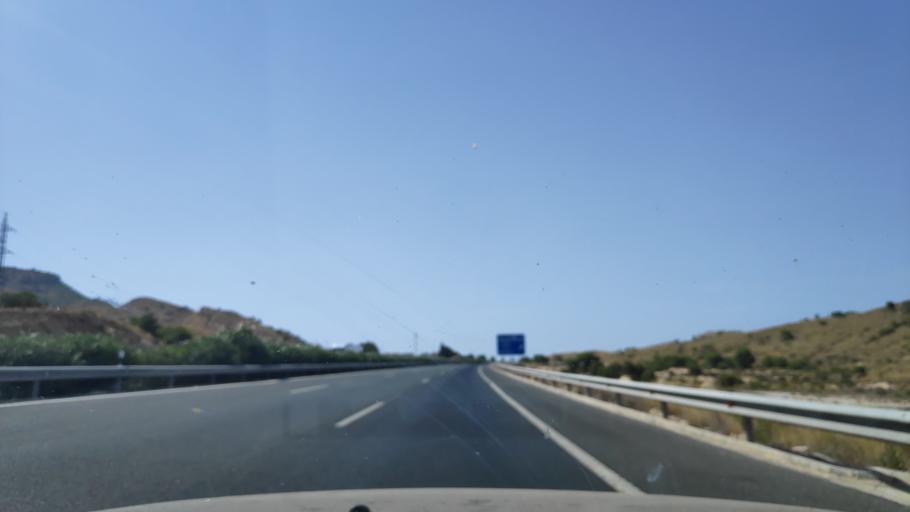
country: ES
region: Murcia
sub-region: Murcia
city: Ulea
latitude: 38.1691
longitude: -1.3090
